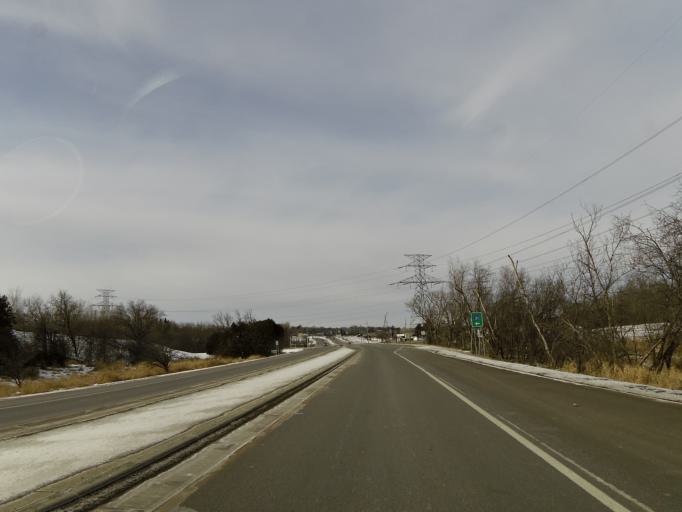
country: US
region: Minnesota
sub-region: Washington County
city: Oak Park Heights
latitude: 45.0301
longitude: -92.7863
